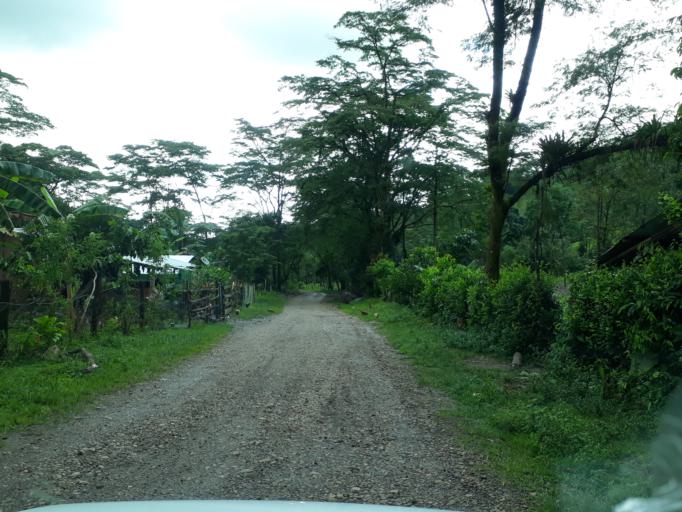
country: CO
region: Cundinamarca
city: Medina
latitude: 4.5834
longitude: -73.3811
